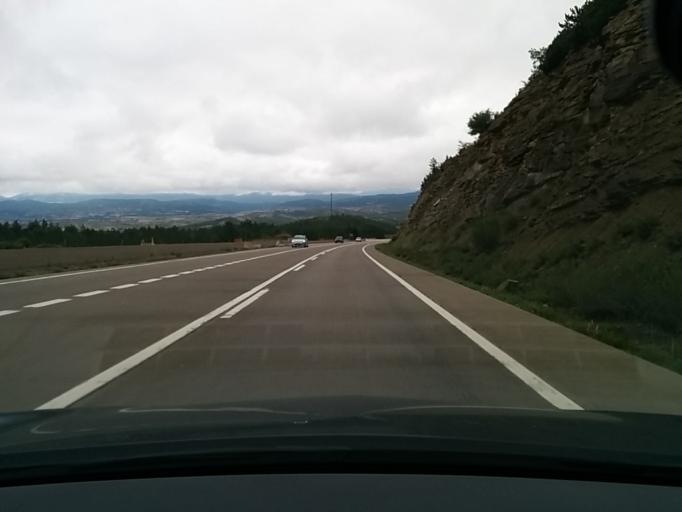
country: ES
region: Aragon
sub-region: Provincia de Huesca
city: Arguis
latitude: 42.3846
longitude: -0.3725
